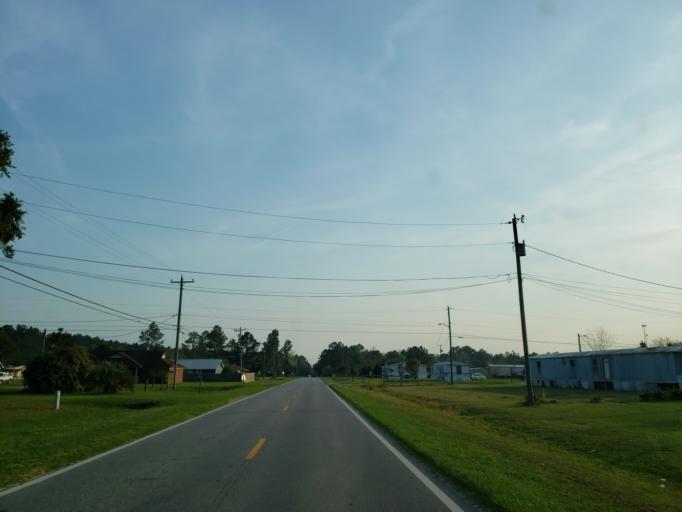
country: US
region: Georgia
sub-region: Cook County
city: Sparks
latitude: 31.1773
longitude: -83.4301
